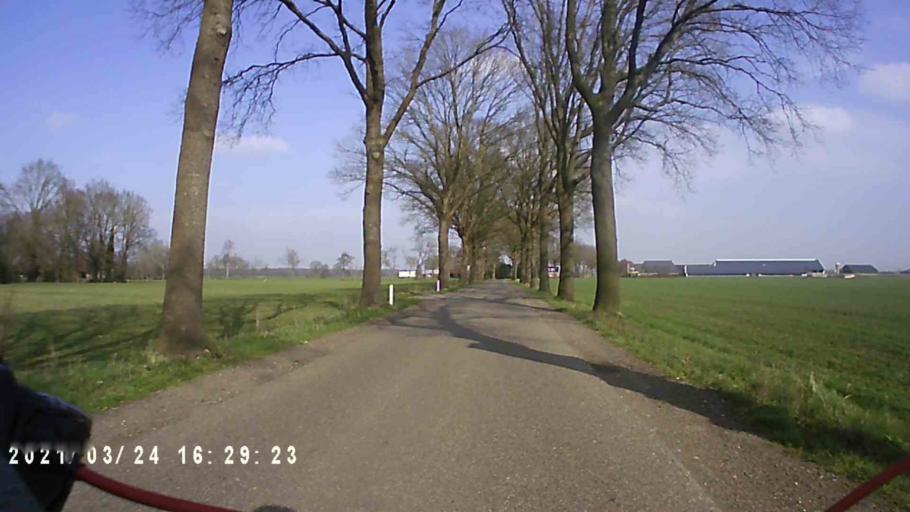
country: NL
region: Groningen
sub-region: Gemeente Leek
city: Leek
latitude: 53.0700
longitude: 6.2787
